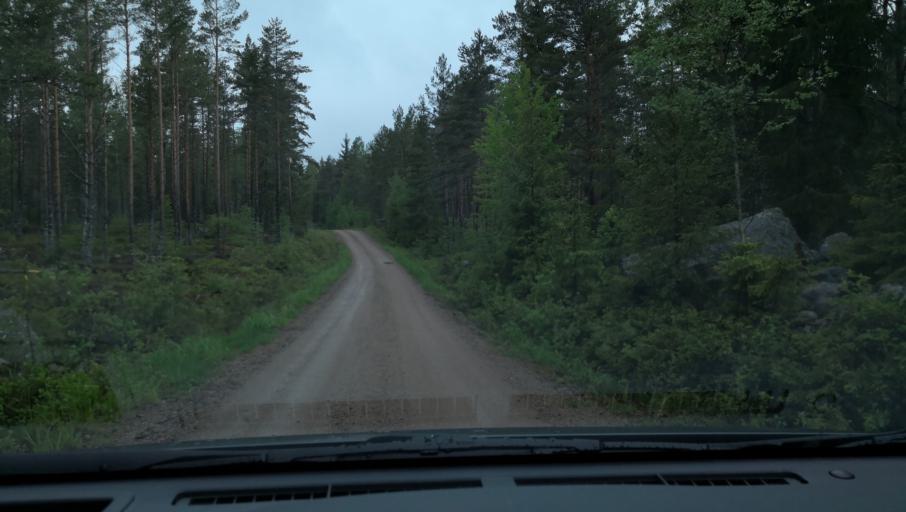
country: SE
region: Uppsala
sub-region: Enkopings Kommun
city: Orsundsbro
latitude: 59.9345
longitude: 17.3237
